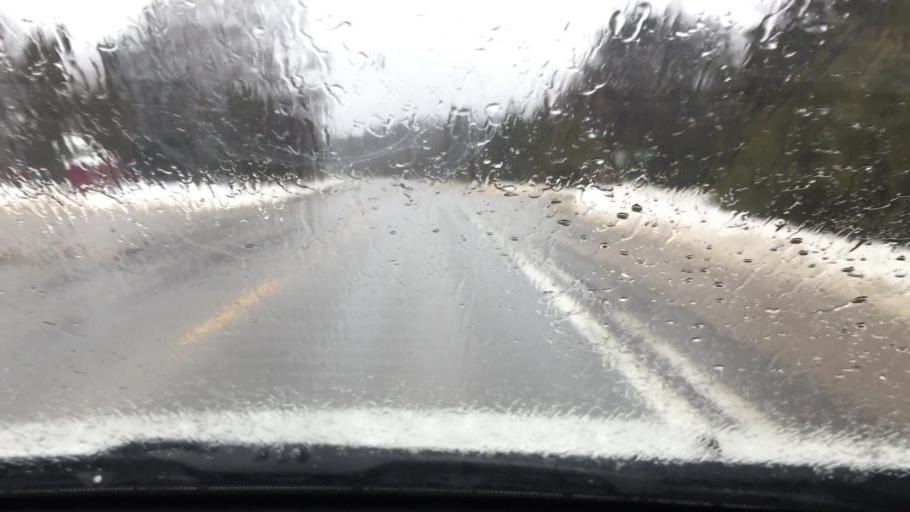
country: US
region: Michigan
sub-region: Charlevoix County
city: Charlevoix
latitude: 45.2592
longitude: -85.1899
